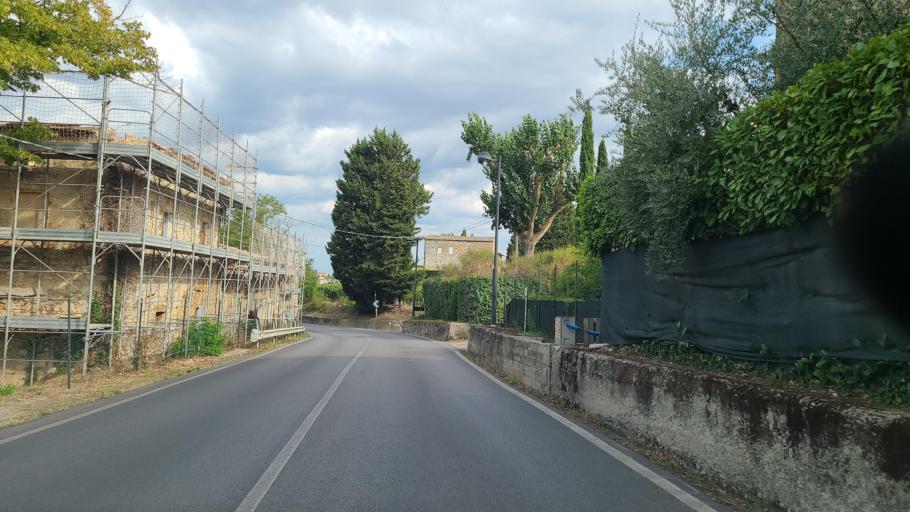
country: IT
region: Tuscany
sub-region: Provincia di Siena
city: San Gimignano
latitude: 43.4783
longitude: 11.0192
